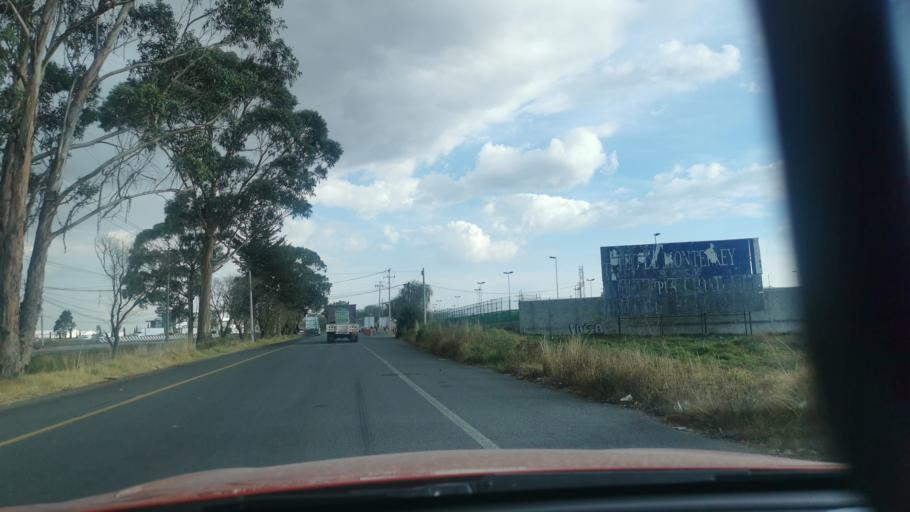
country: MX
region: Mexico
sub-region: Toluca
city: Colonia Aviacion Autopan
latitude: 19.3827
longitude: -99.7067
